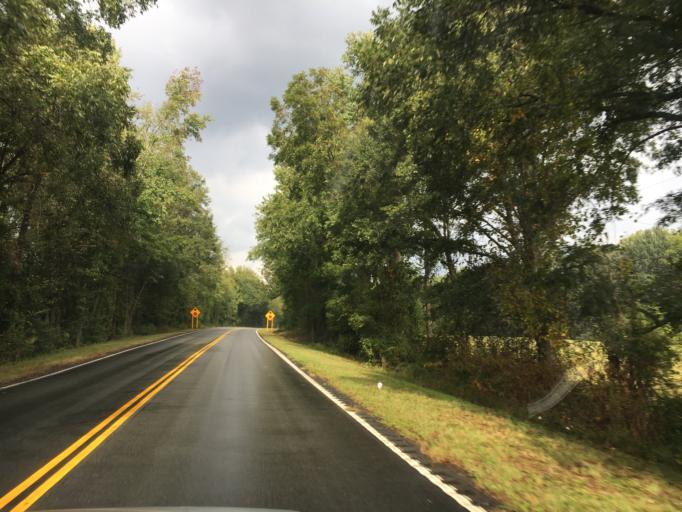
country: US
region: Georgia
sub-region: Hart County
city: Reed Creek
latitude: 34.4042
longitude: -82.8004
